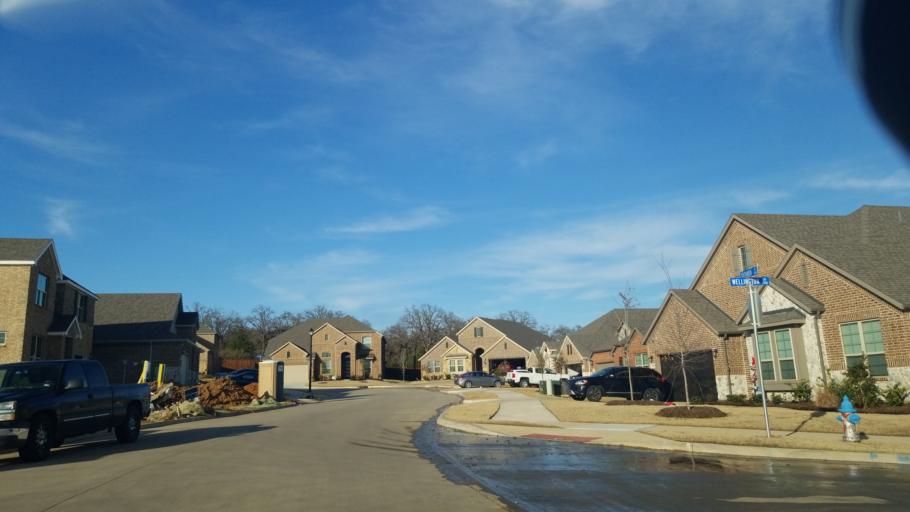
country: US
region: Texas
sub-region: Denton County
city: Corinth
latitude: 33.1462
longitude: -97.0762
